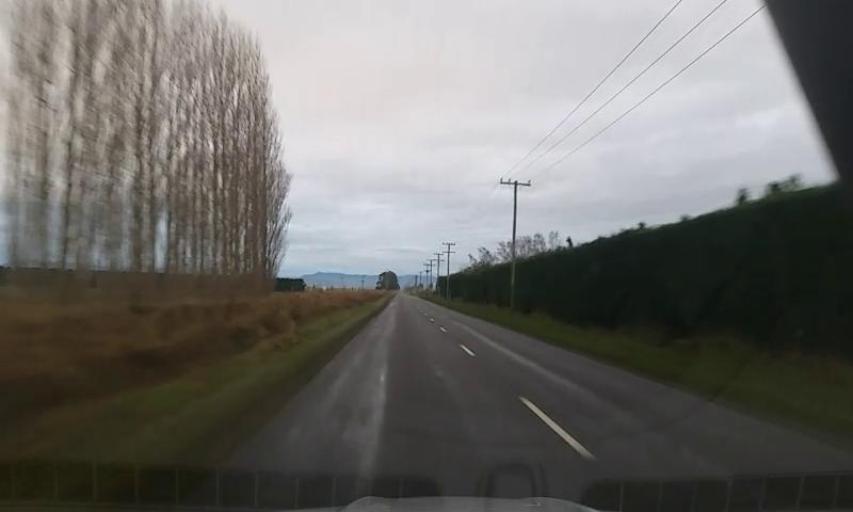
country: NZ
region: Canterbury
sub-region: Ashburton District
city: Methven
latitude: -43.7408
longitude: 171.6982
